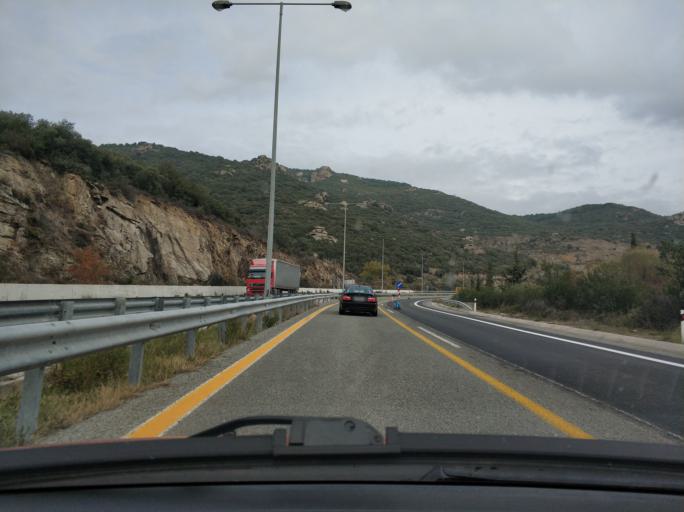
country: GR
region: East Macedonia and Thrace
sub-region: Nomos Kavalas
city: Palaio Tsifliki
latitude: 40.9078
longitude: 24.3429
